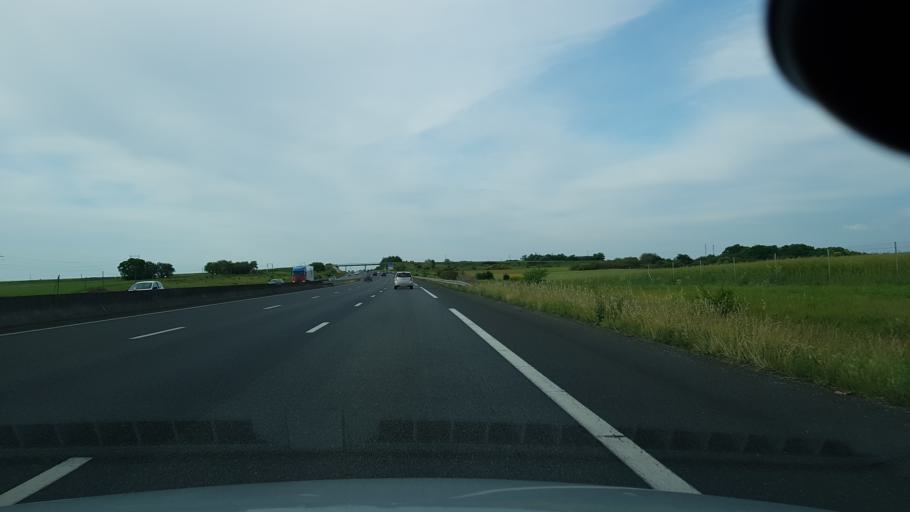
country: FR
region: Centre
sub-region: Departement du Loir-et-Cher
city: Suevres
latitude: 47.6922
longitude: 1.4340
